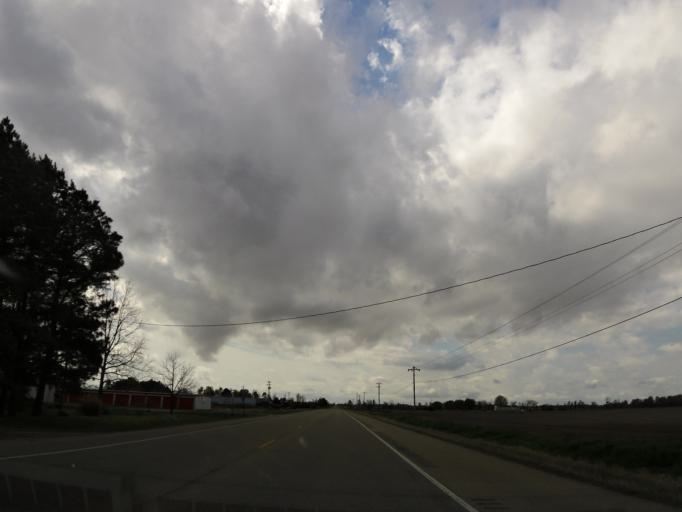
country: US
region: Arkansas
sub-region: Clay County
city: Corning
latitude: 36.4432
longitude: -90.5857
